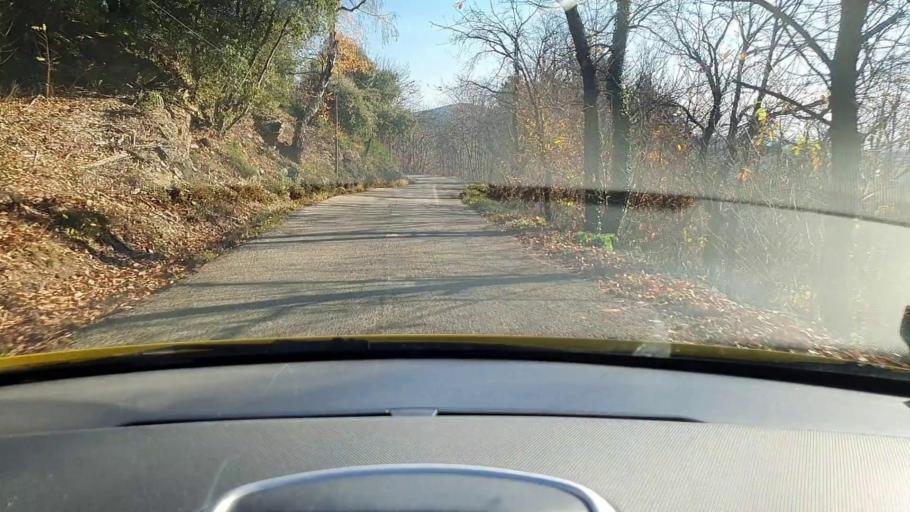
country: FR
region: Languedoc-Roussillon
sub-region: Departement du Gard
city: Branoux-les-Taillades
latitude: 44.2822
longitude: 3.9506
